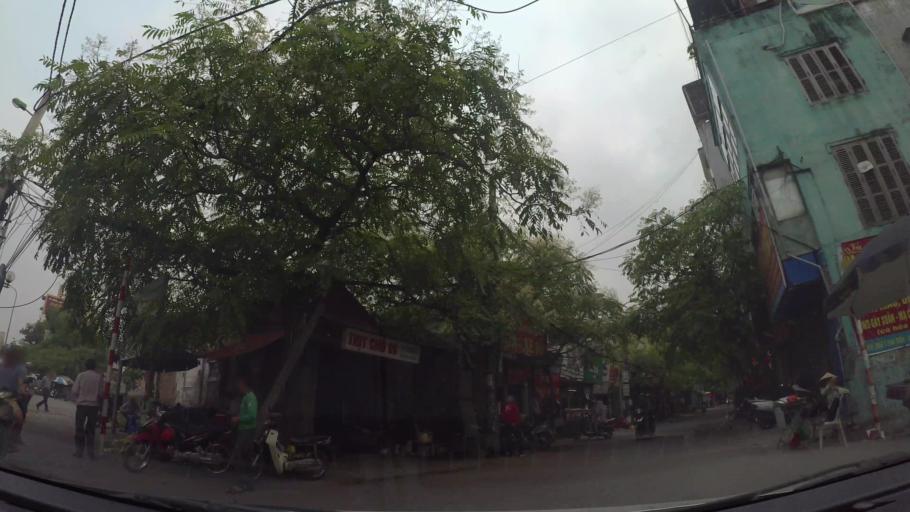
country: VN
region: Ha Noi
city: Cau Dien
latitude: 21.0416
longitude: 105.7609
